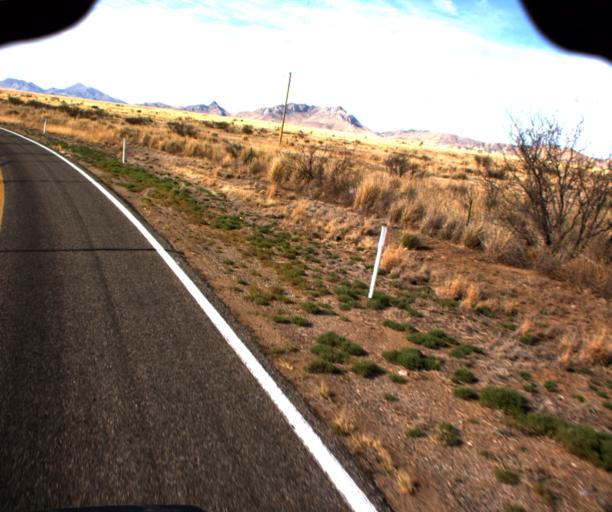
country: US
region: Arizona
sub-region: Cochise County
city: Willcox
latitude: 32.0215
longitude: -109.4401
